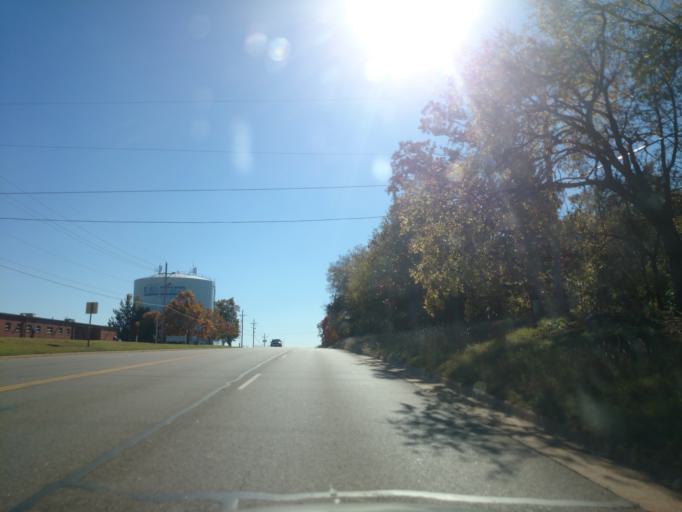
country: US
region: Oklahoma
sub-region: Payne County
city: Stillwater
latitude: 36.1504
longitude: -97.0697
